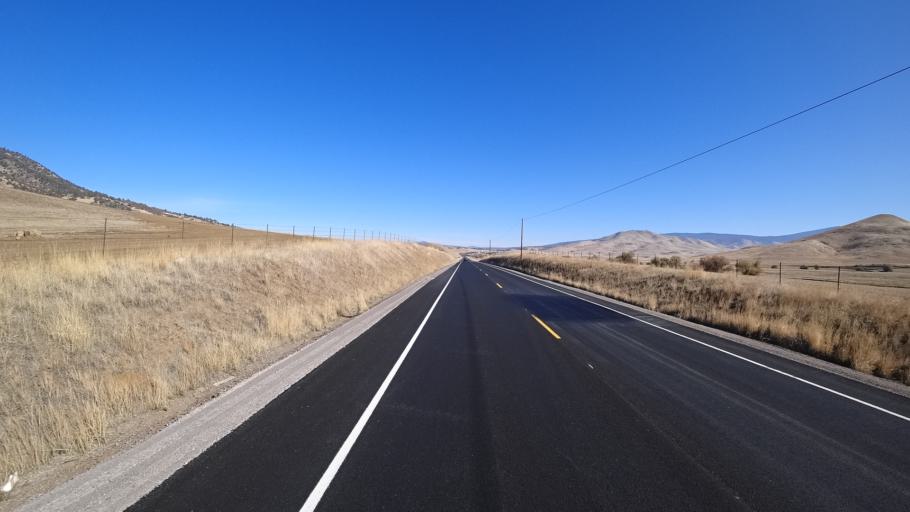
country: US
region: California
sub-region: Siskiyou County
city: Montague
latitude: 41.8305
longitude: -122.4913
